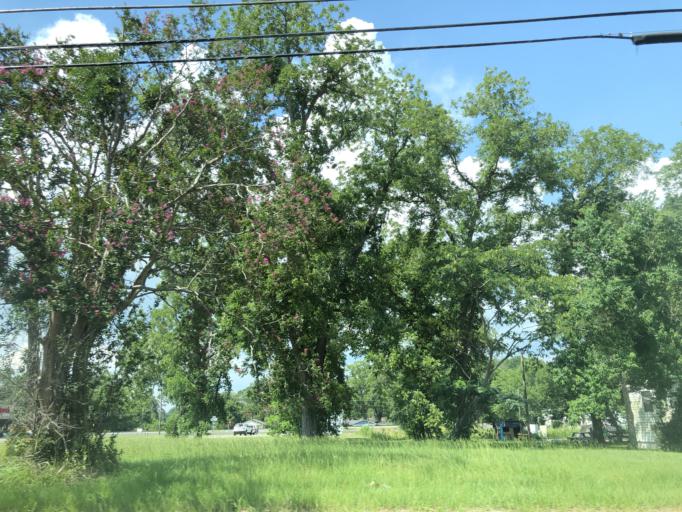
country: US
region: Georgia
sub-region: Telfair County
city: McRae
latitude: 32.0656
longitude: -82.8932
